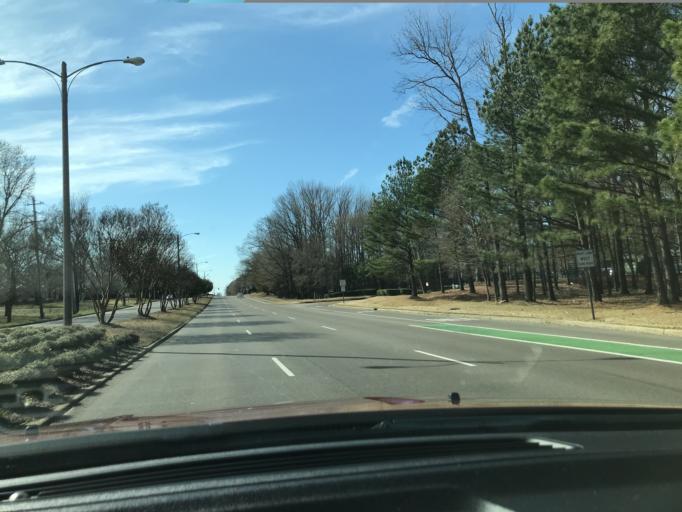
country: US
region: Tennessee
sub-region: Shelby County
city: Germantown
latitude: 35.0482
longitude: -89.7862
